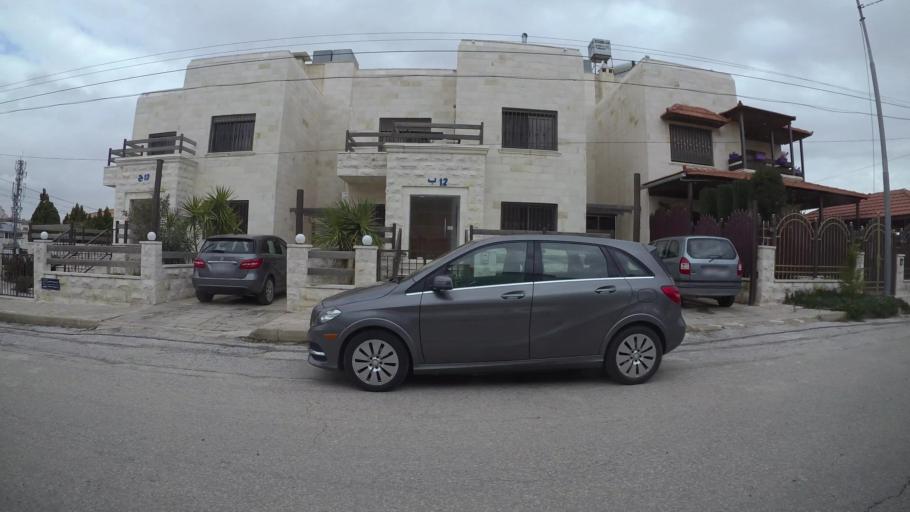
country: JO
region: Amman
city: Wadi as Sir
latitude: 31.9881
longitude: 35.8353
